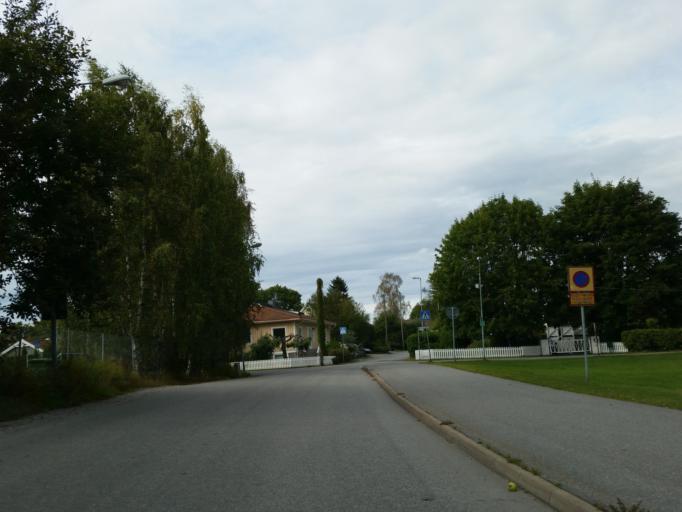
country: SE
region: Stockholm
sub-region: Sollentuna Kommun
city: Sollentuna
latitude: 59.4526
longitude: 17.9291
